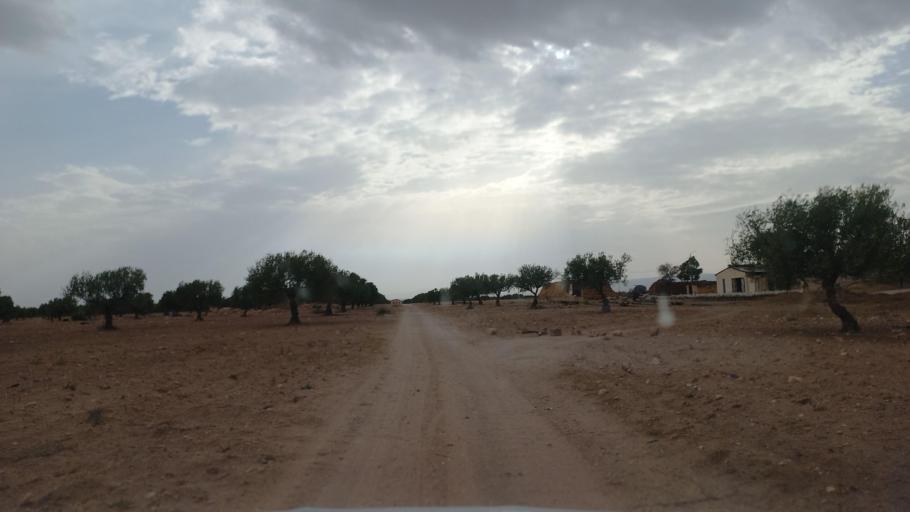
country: TN
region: Al Qasrayn
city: Sbiba
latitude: 35.2974
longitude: 9.0832
